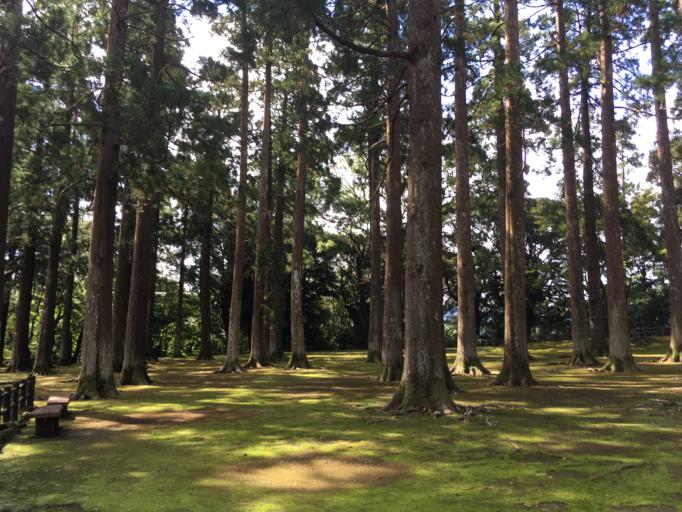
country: JP
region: Miyazaki
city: Nichinan
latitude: 31.6292
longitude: 131.3505
